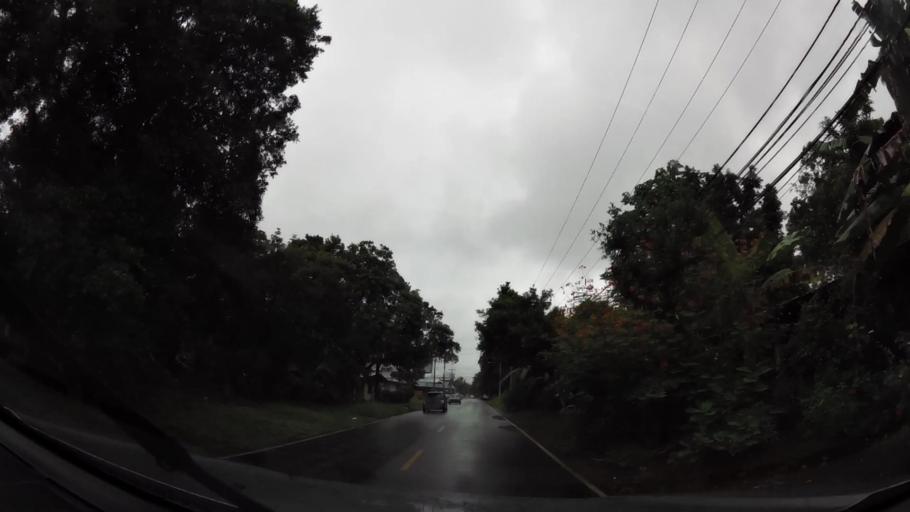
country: PA
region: Chiriqui
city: David
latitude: 8.4375
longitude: -82.4354
